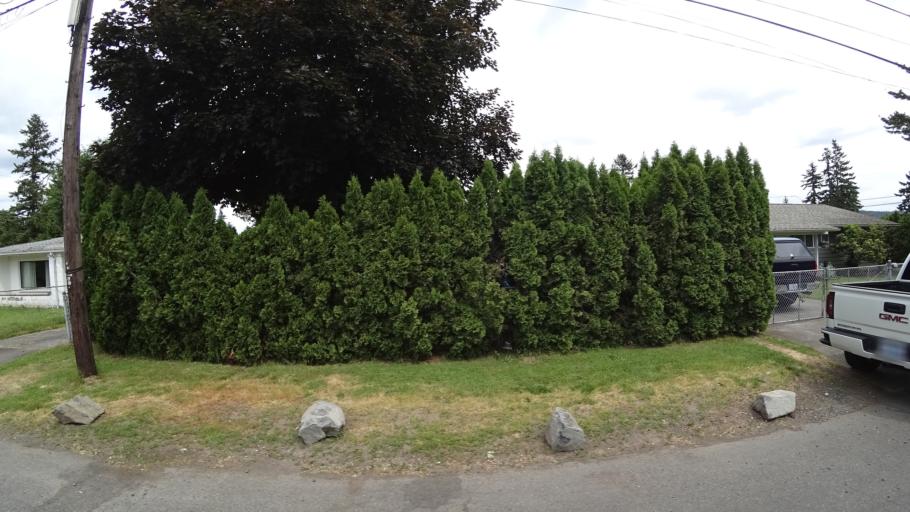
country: US
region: Oregon
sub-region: Multnomah County
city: Lents
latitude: 45.4888
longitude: -122.5420
